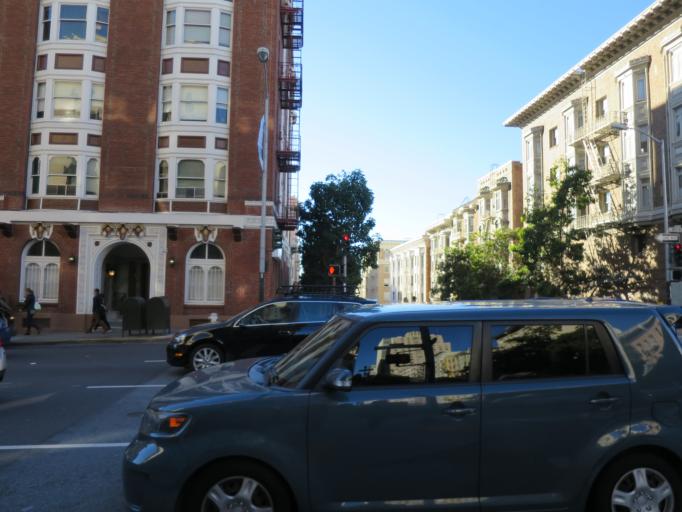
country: US
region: California
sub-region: San Francisco County
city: San Francisco
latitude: 37.7897
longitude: -122.4137
